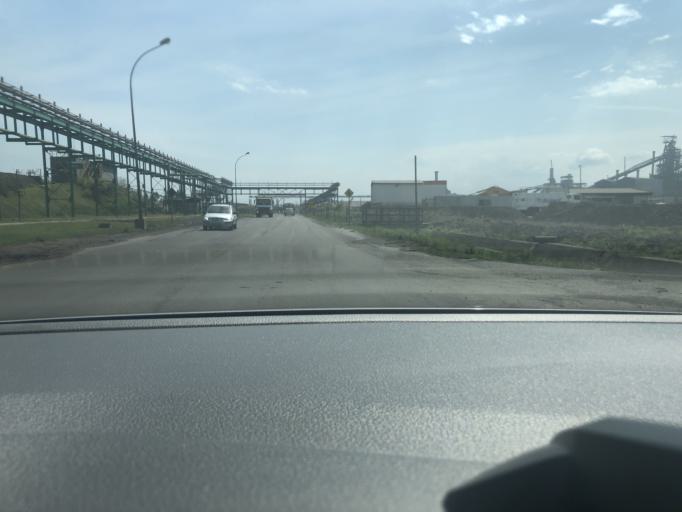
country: BR
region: Rio de Janeiro
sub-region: Itaguai
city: Itaguai
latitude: -22.9117
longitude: -43.7311
